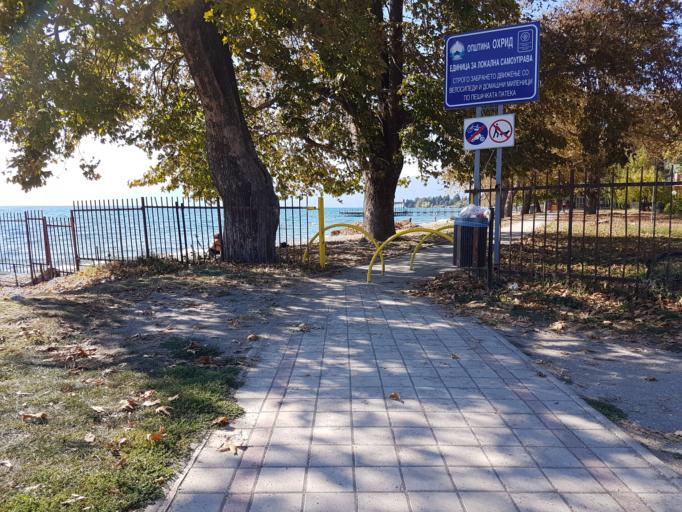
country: MK
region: Ohrid
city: Ohrid
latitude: 41.1184
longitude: 20.7859
